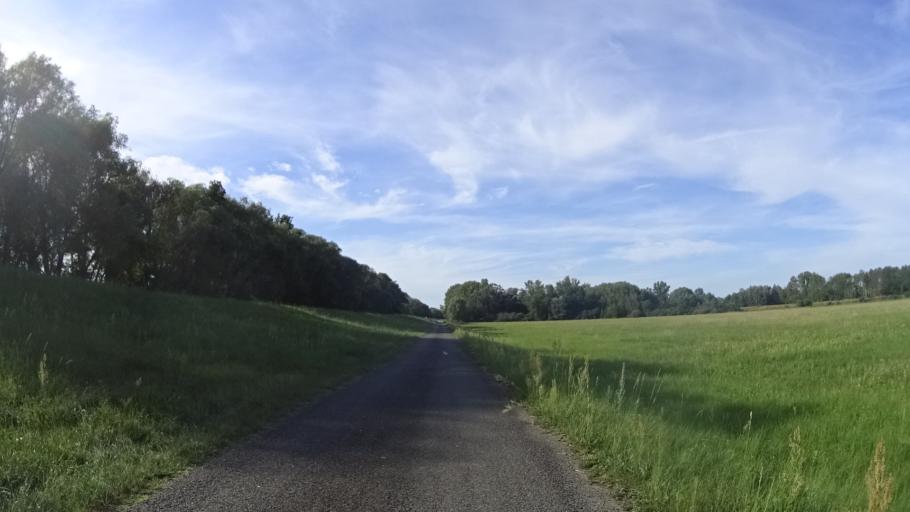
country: AT
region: Lower Austria
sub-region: Politischer Bezirk Ganserndorf
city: Drosing
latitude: 48.5502
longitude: 16.9627
